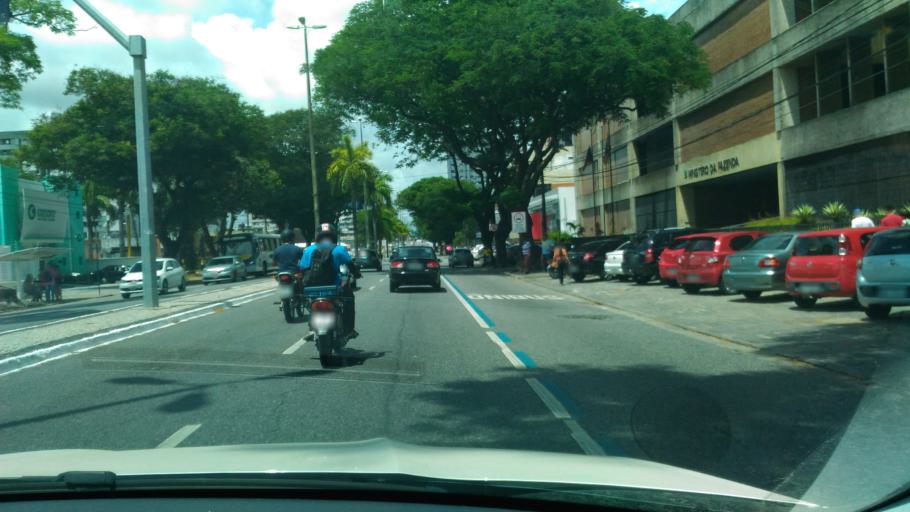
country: BR
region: Paraiba
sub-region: Joao Pessoa
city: Joao Pessoa
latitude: -7.1197
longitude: -34.8554
